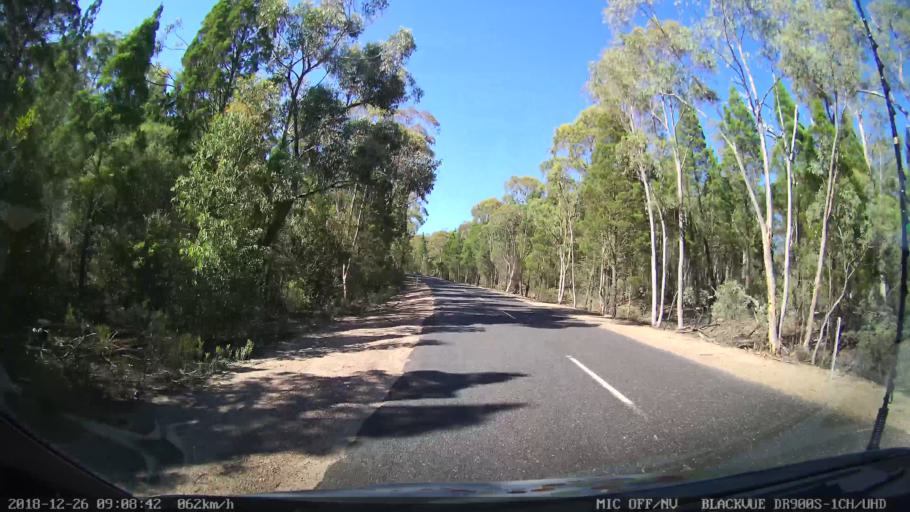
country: AU
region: New South Wales
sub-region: Mid-Western Regional
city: Kandos
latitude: -32.7178
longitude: 150.0003
